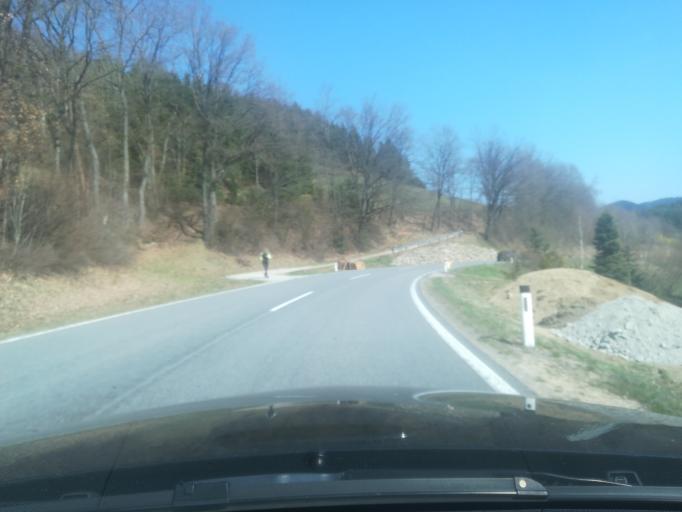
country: AT
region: Upper Austria
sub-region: Politischer Bezirk Perg
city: Bad Kreuzen
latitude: 48.4169
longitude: 14.7518
